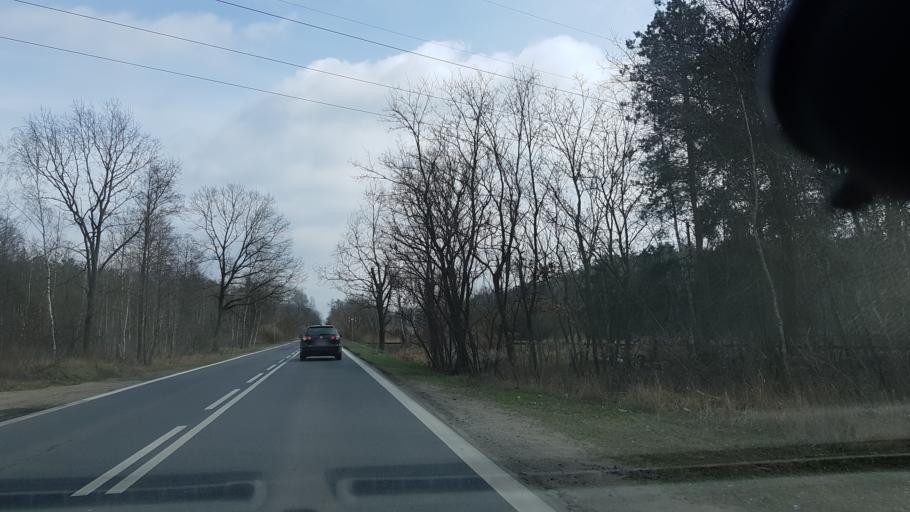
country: PL
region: Masovian Voivodeship
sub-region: Warszawa
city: Rembertow
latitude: 52.2560
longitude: 21.1920
